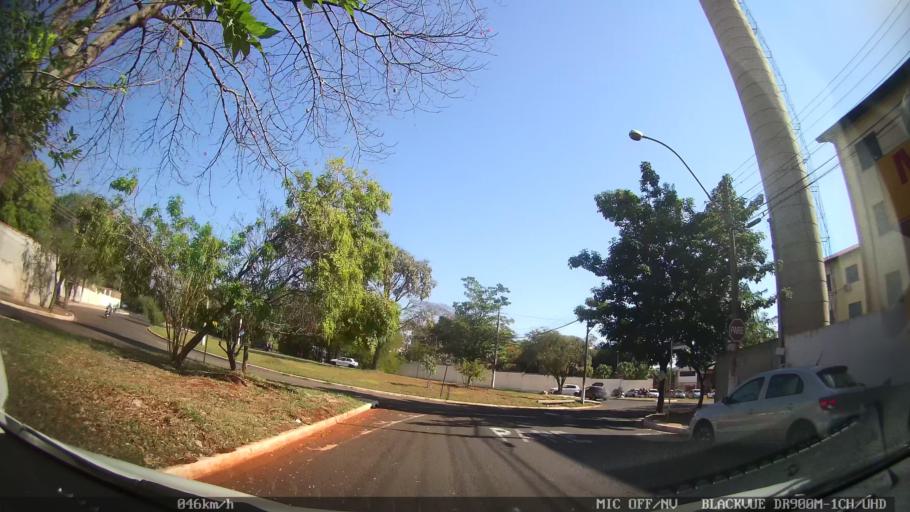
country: BR
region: Sao Paulo
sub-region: Ribeirao Preto
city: Ribeirao Preto
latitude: -21.2132
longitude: -47.8272
